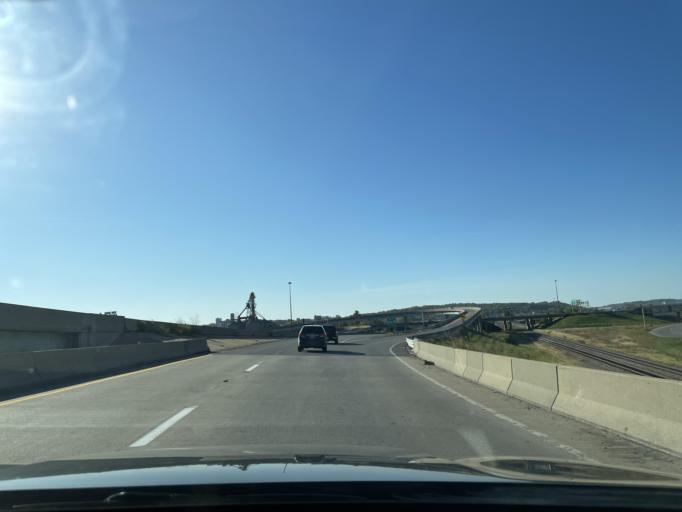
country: US
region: Missouri
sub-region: Buchanan County
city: Saint Joseph
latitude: 39.7521
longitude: -94.8540
